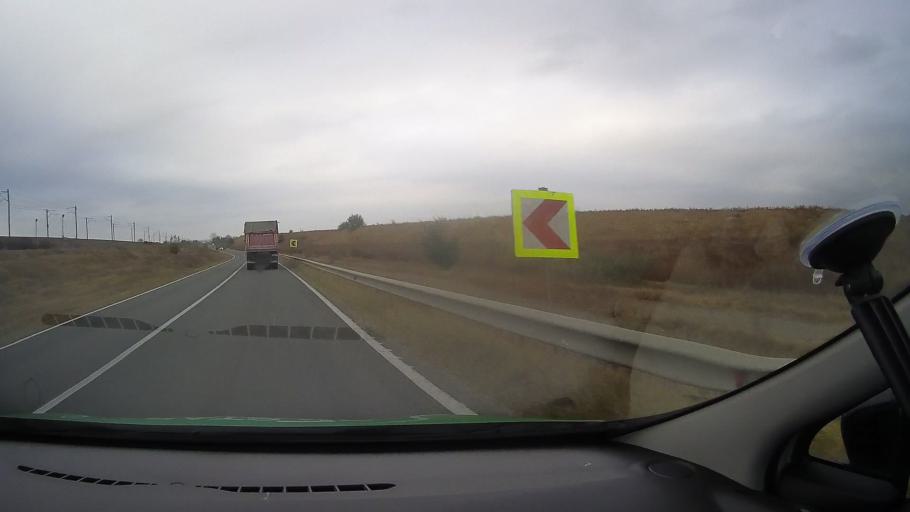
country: RO
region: Constanta
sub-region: Comuna Poarta Alba
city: Poarta Alba
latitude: 44.2213
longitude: 28.3874
